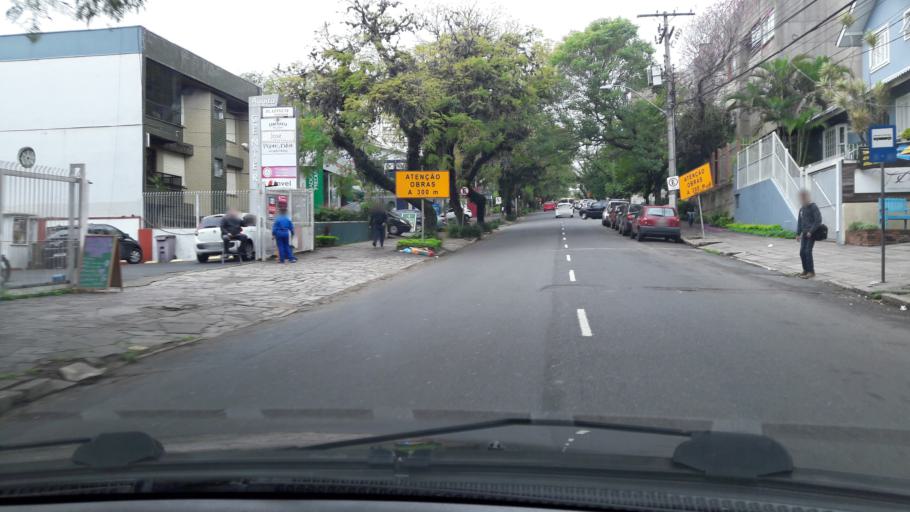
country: BR
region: Rio Grande do Sul
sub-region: Porto Alegre
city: Porto Alegre
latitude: -30.0268
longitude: -51.1891
